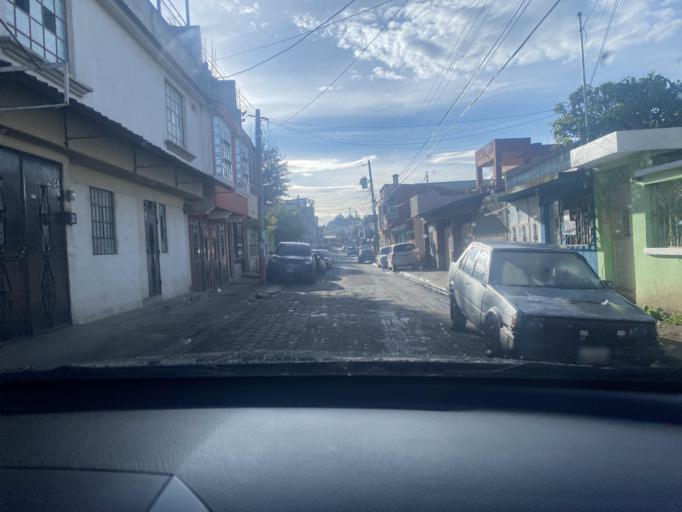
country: GT
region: Quetzaltenango
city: Olintepeque
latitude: 14.8640
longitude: -91.5205
